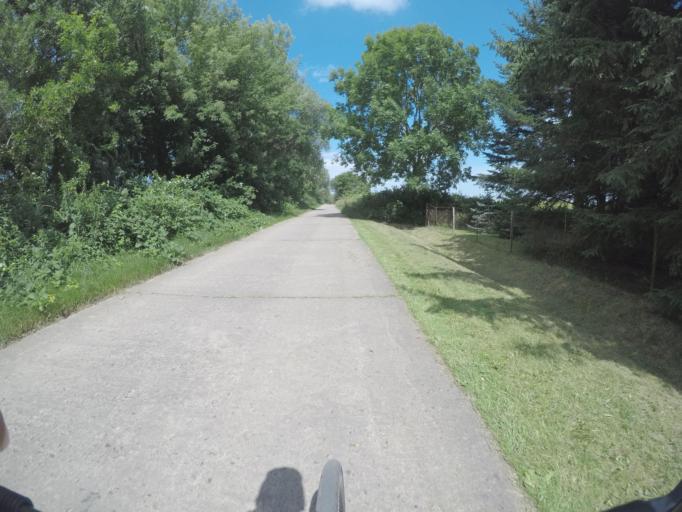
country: DE
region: Mecklenburg-Vorpommern
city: Altefahr
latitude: 54.3341
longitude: 13.1287
